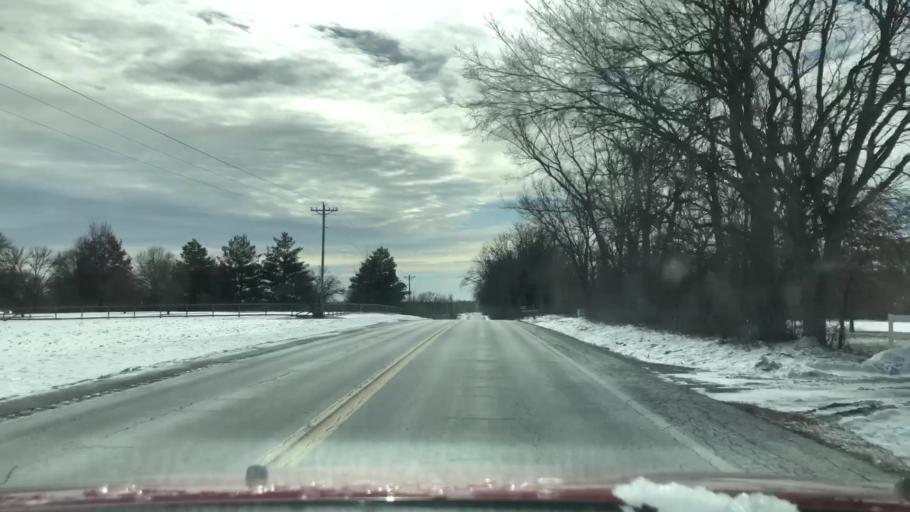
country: US
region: Missouri
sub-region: Jackson County
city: Lone Jack
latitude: 38.8830
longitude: -94.1349
